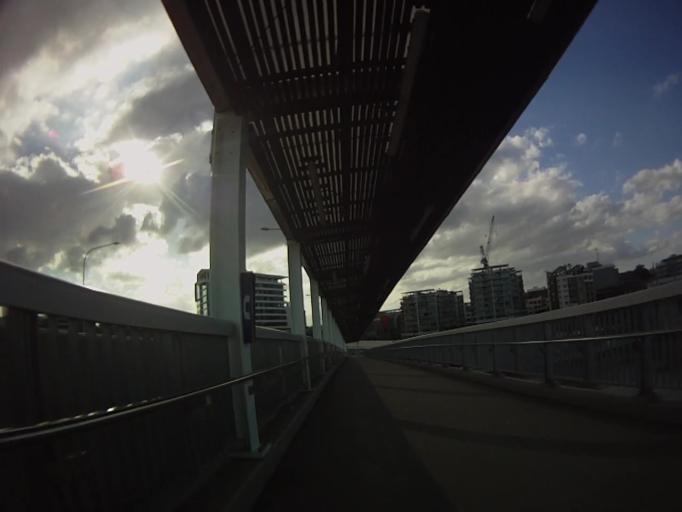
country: AU
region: Queensland
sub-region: Brisbane
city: Milton
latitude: -27.4698
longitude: 153.0124
